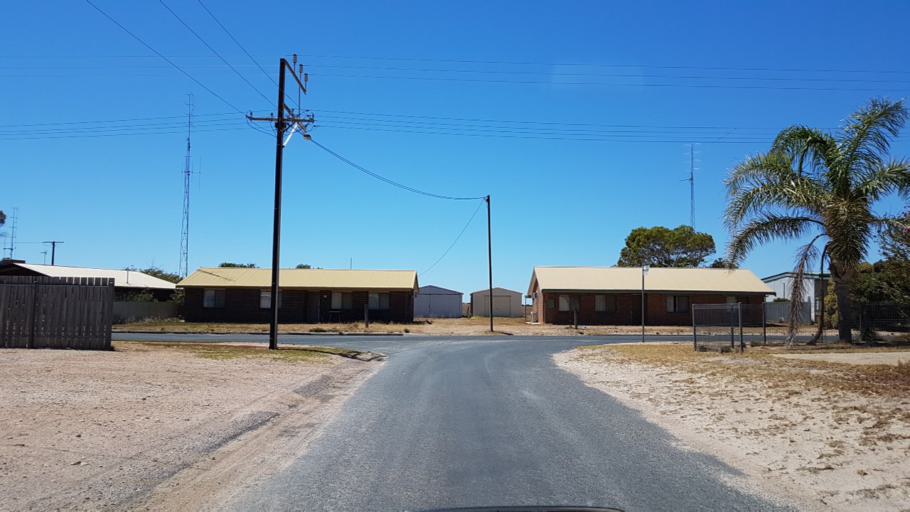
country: AU
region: South Australia
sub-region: Copper Coast
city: Wallaroo
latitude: -33.8985
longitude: 137.6297
